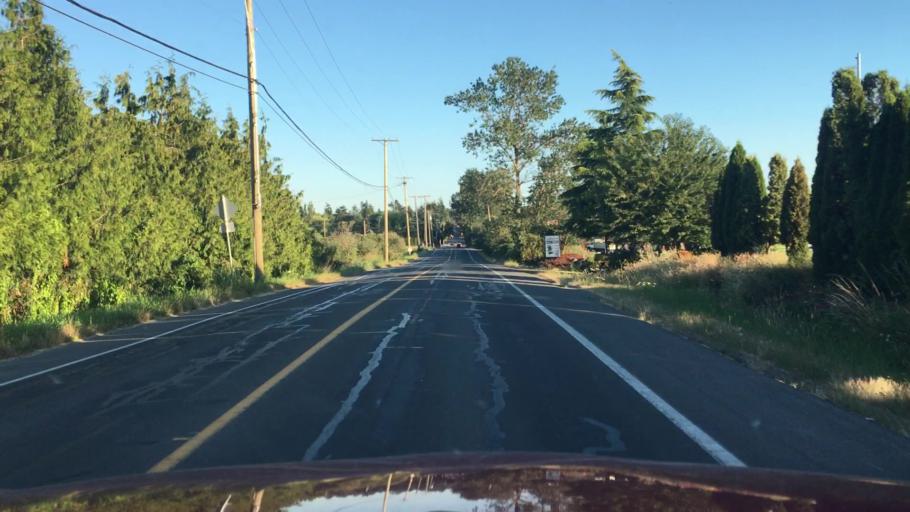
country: CA
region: British Columbia
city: Victoria
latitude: 48.4764
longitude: -123.3525
